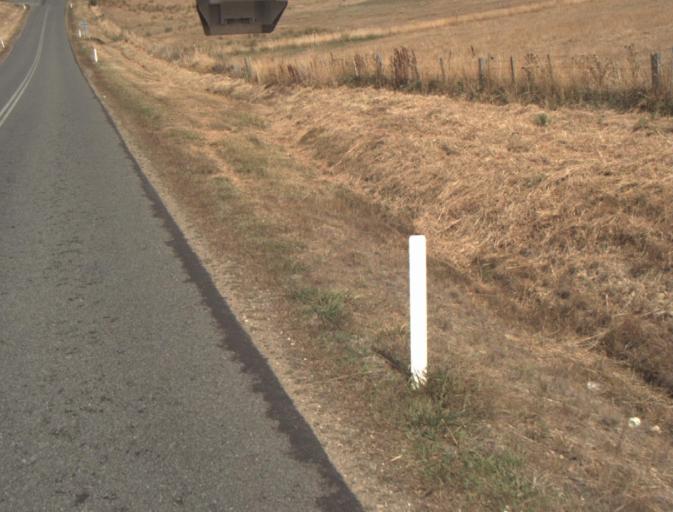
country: AU
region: Tasmania
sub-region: Launceston
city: Mayfield
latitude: -41.2083
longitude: 147.1189
